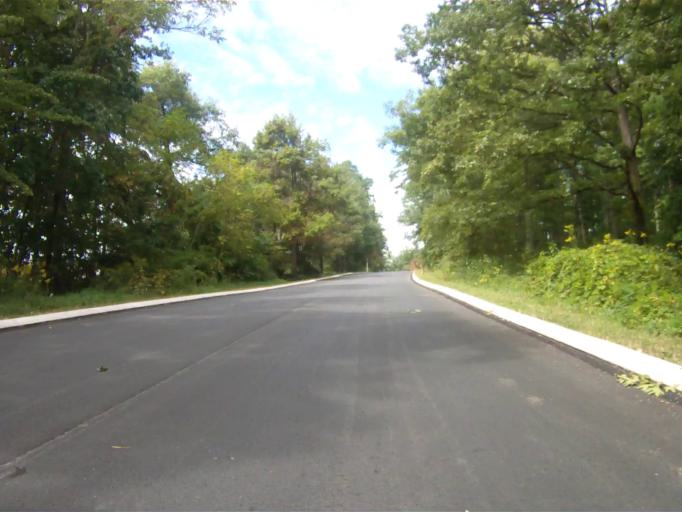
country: US
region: Pennsylvania
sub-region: Centre County
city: Park Forest Village
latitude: 40.8057
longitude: -77.9210
